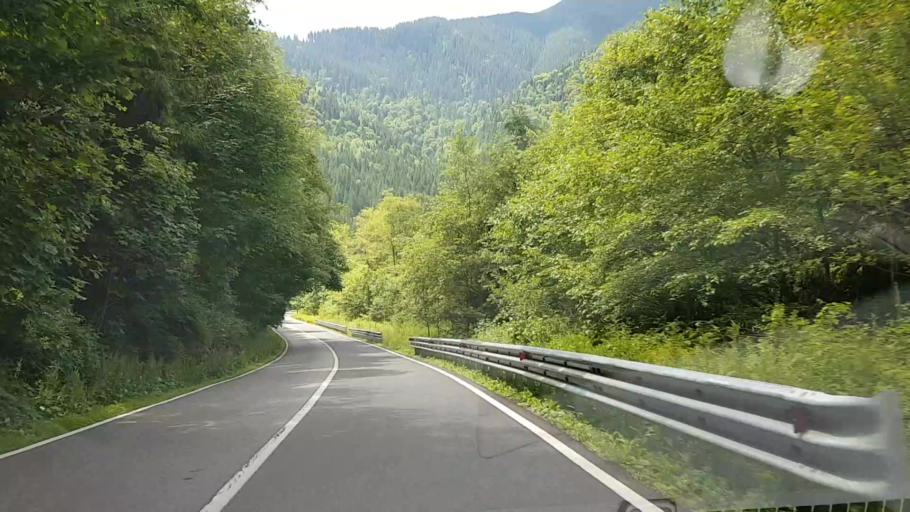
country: RO
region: Suceava
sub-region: Comuna Crucea
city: Crucea
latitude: 47.3851
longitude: 25.5786
